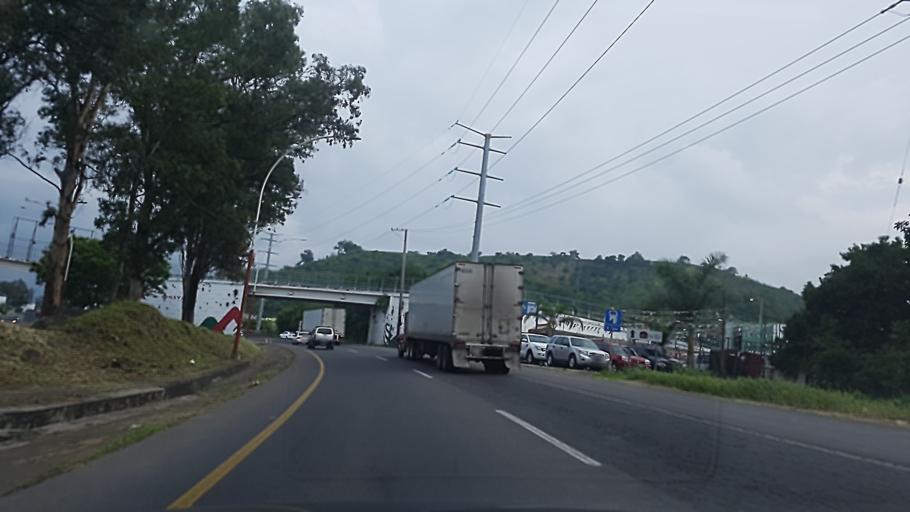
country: MX
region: Nayarit
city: Tepic
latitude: 21.4872
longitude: -104.9036
